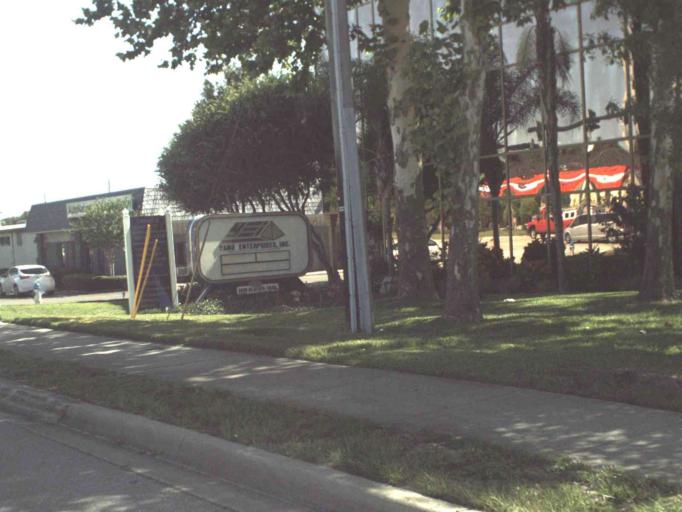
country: US
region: Florida
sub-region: Seminole County
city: Oviedo
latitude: 28.6496
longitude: -81.2082
